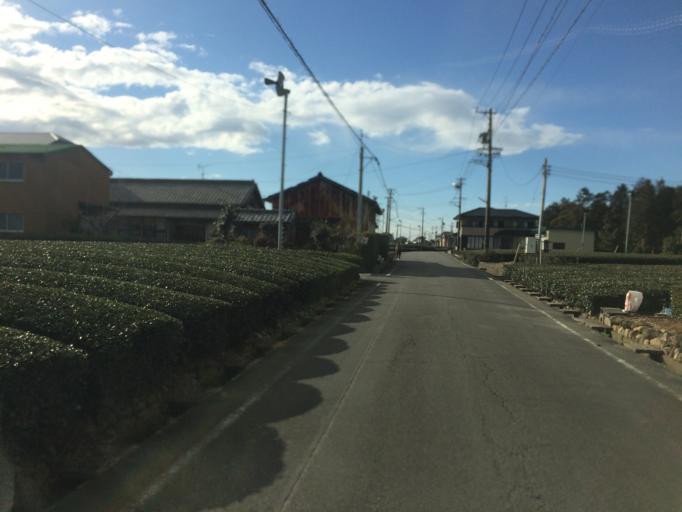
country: JP
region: Shizuoka
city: Kanaya
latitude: 34.7635
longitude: 138.1486
